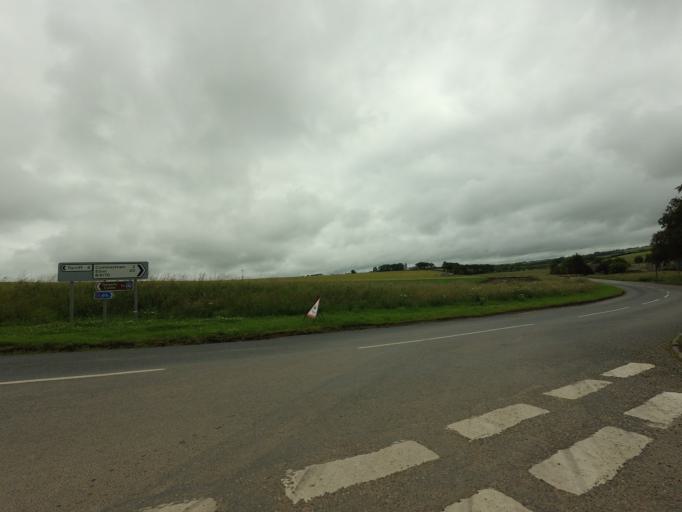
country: GB
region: Scotland
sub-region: Aberdeenshire
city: Turriff
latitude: 57.5419
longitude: -2.3659
